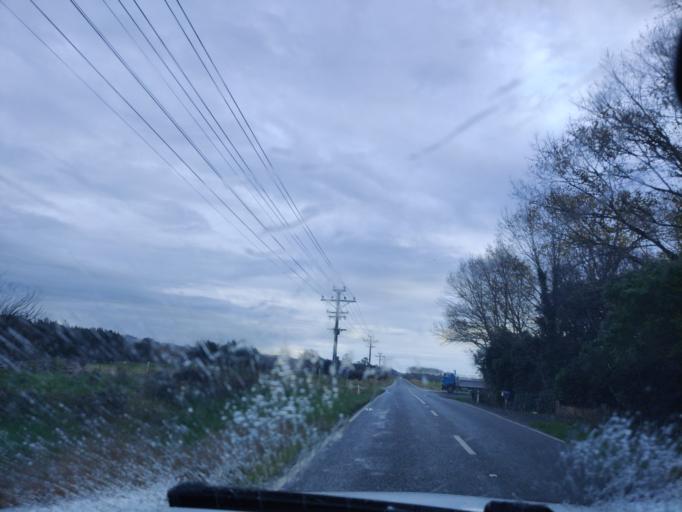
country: NZ
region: Manawatu-Wanganui
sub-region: Palmerston North City
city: Palmerston North
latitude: -40.3482
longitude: 175.7029
